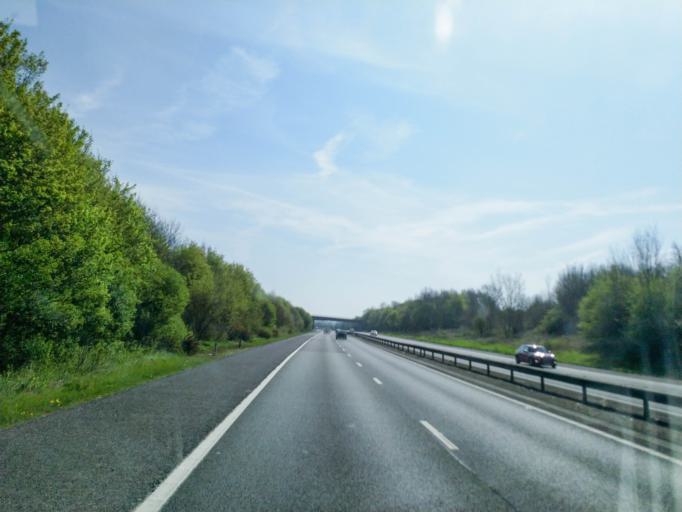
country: GB
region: England
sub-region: Kent
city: Kemsing
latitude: 51.3030
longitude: 0.2105
